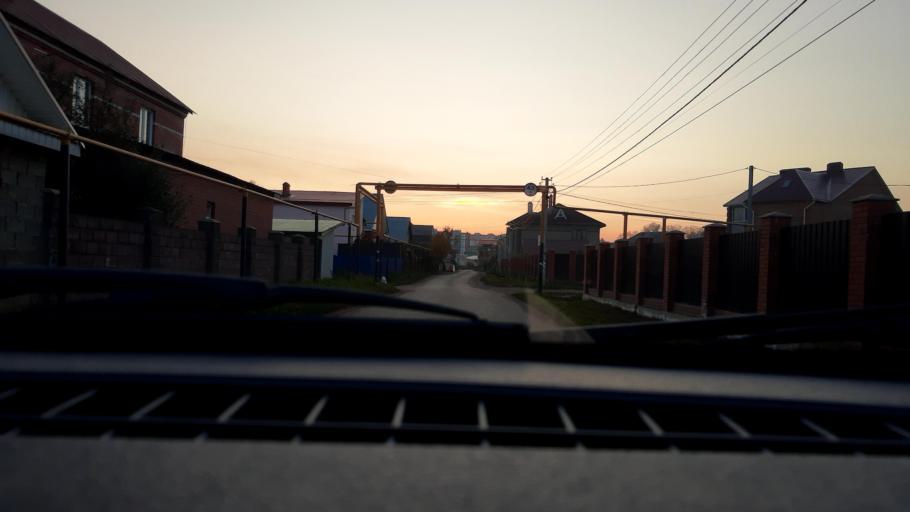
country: RU
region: Bashkortostan
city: Mikhaylovka
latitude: 54.7820
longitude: 55.9023
